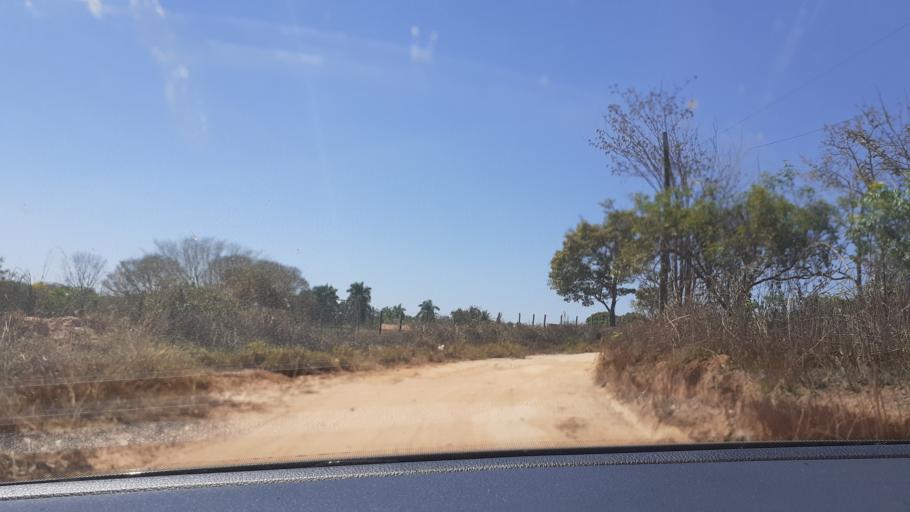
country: BR
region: Goias
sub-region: Caldas Novas
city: Caldas Novas
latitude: -17.7401
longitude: -48.6551
